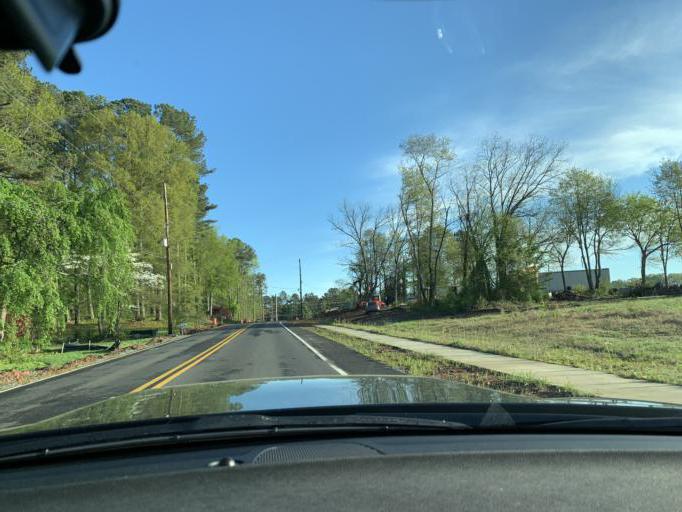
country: US
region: Georgia
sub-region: Fulton County
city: Roswell
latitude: 34.0665
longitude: -84.3743
